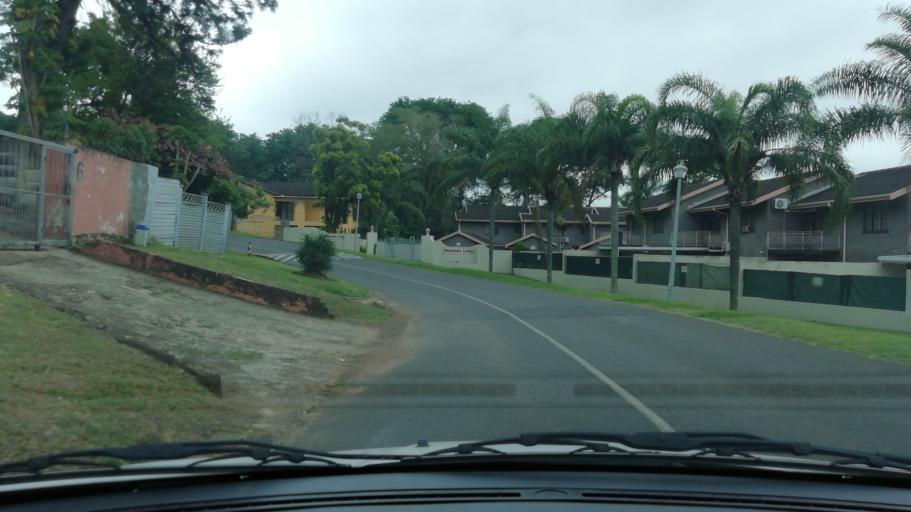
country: ZA
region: KwaZulu-Natal
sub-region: uThungulu District Municipality
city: Empangeni
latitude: -28.7591
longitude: 31.8912
